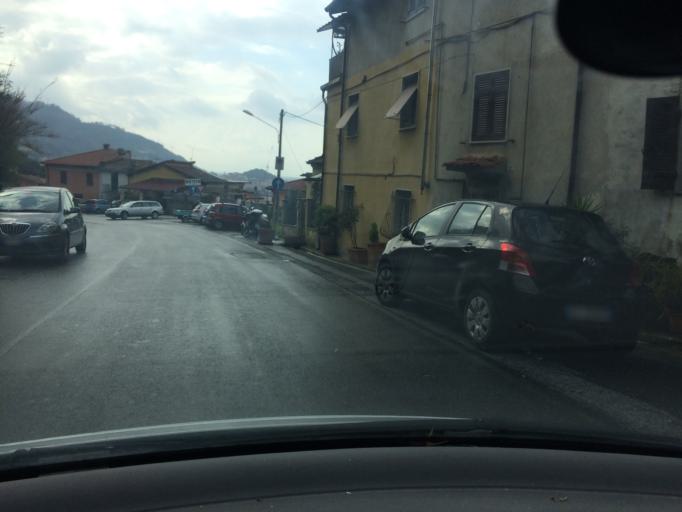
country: IT
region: Tuscany
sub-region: Provincia di Massa-Carrara
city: Massa
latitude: 44.0516
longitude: 10.1271
